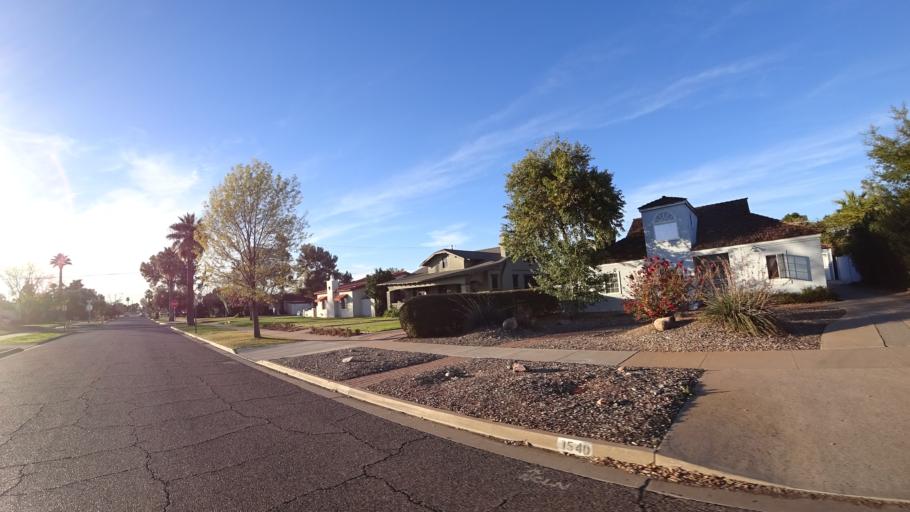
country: US
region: Arizona
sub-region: Maricopa County
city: Phoenix
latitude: 33.4741
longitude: -112.0931
